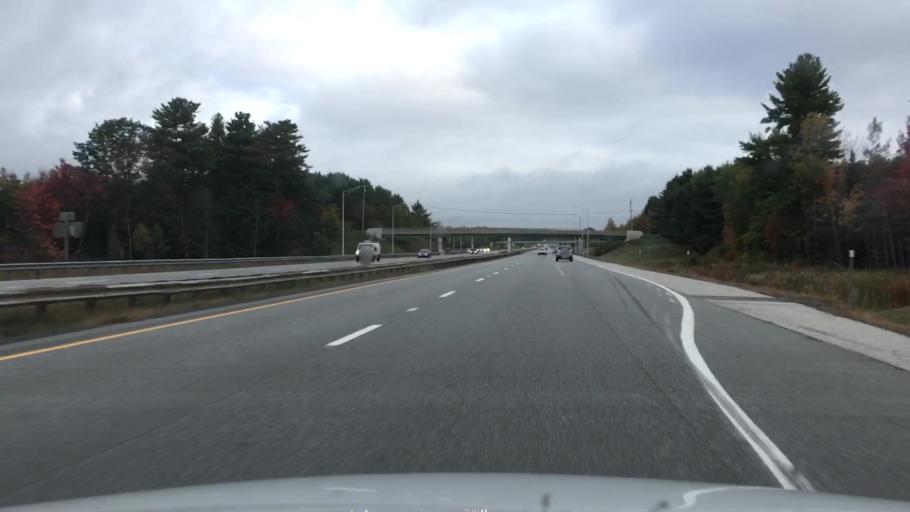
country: US
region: Maine
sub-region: Cumberland County
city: New Gloucester
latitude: 43.8768
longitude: -70.3320
